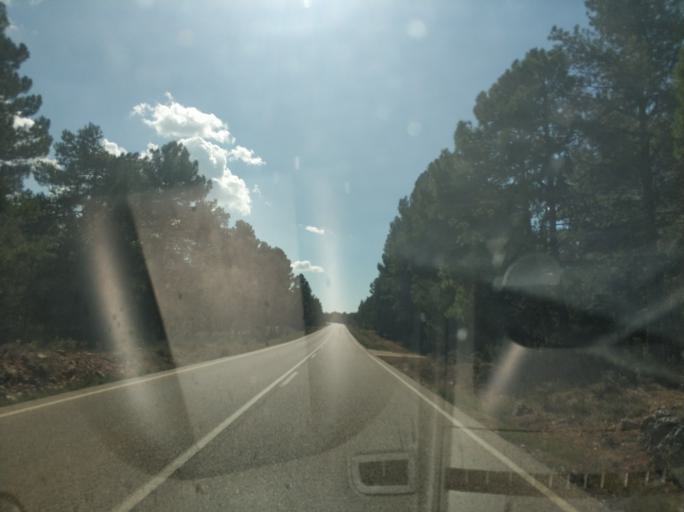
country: ES
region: Castille and Leon
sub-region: Provincia de Soria
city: Ucero
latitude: 41.7425
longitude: -3.0449
